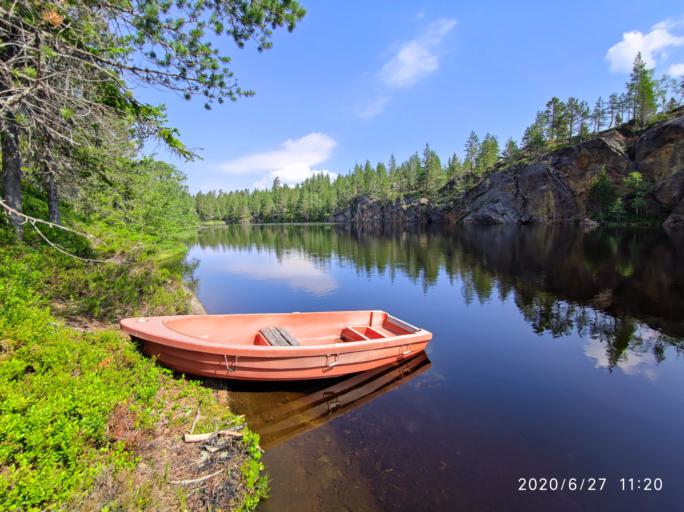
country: NO
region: Buskerud
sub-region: Kongsberg
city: Kongsberg
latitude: 59.6570
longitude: 9.5860
